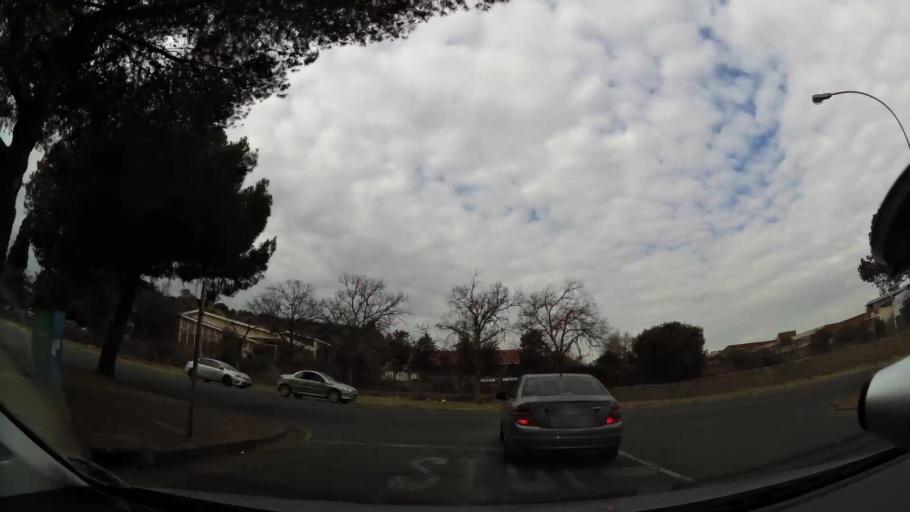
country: ZA
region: Orange Free State
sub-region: Mangaung Metropolitan Municipality
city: Bloemfontein
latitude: -29.1089
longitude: 26.2133
